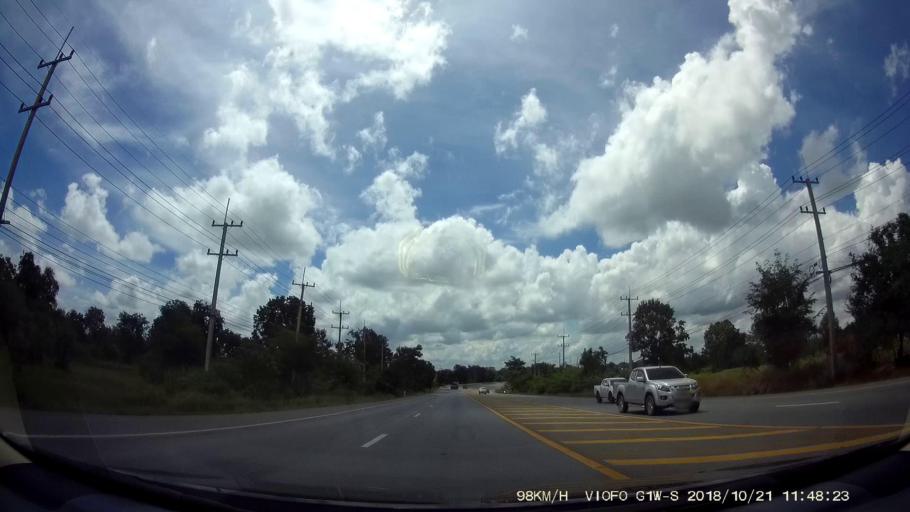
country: TH
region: Chaiyaphum
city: Noen Sa-nga
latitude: 15.6480
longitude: 101.9502
